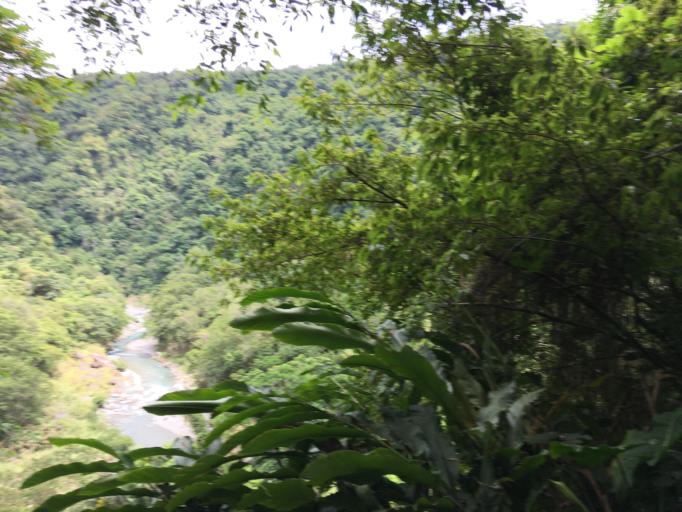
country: TW
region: Taiwan
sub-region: Yilan
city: Yilan
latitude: 24.4236
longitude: 121.6950
